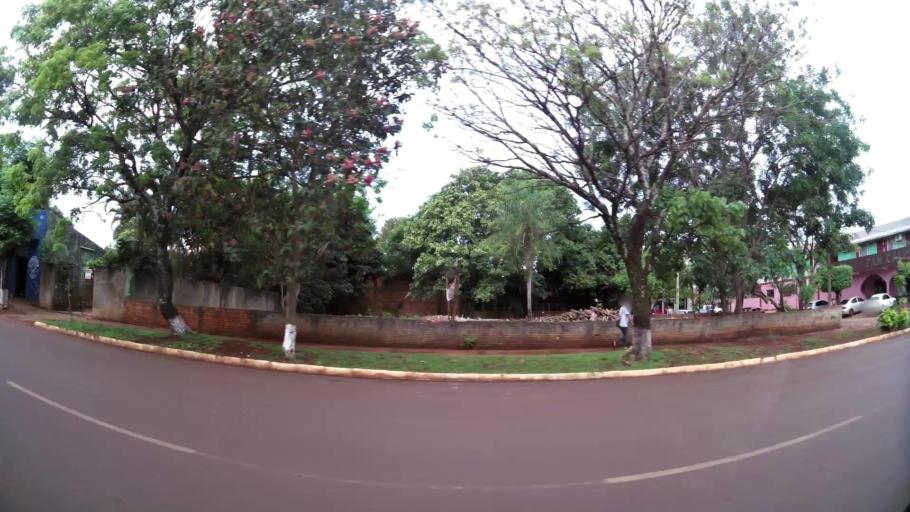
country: PY
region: Alto Parana
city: Ciudad del Este
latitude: -25.4019
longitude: -54.6418
